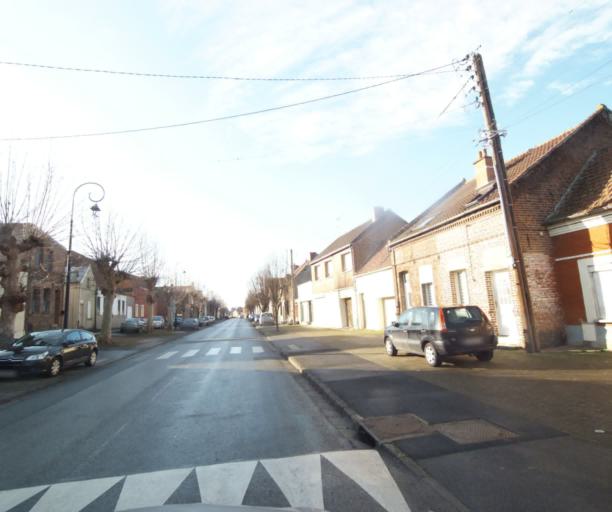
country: FR
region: Nord-Pas-de-Calais
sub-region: Departement du Nord
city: Maing
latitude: 50.3101
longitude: 3.4876
